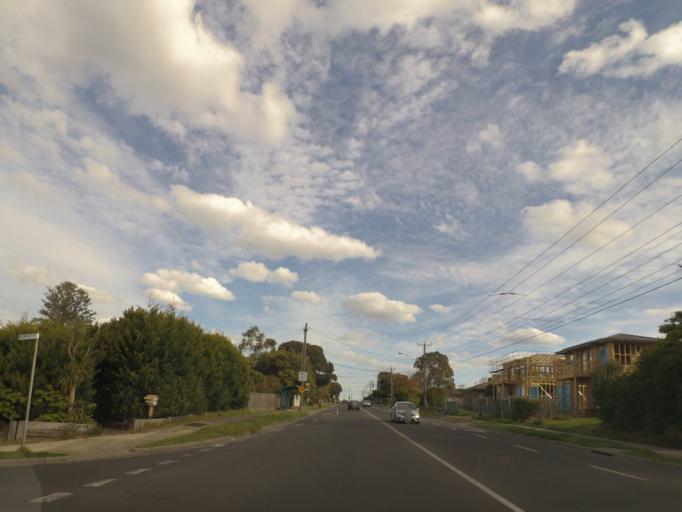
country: AU
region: Victoria
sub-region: Manningham
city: Doncaster East
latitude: -37.7845
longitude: 145.1442
